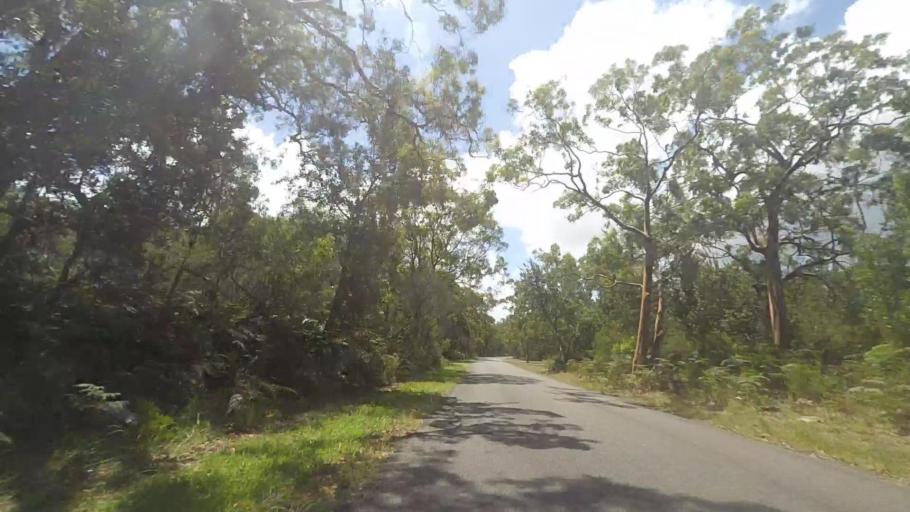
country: AU
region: New South Wales
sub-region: Great Lakes
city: Bulahdelah
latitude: -32.5099
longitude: 152.3189
